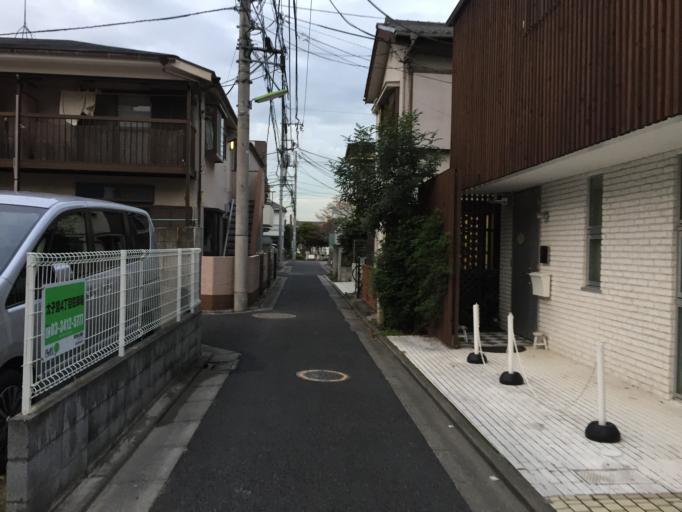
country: JP
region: Tokyo
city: Tokyo
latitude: 35.6435
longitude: 139.6668
